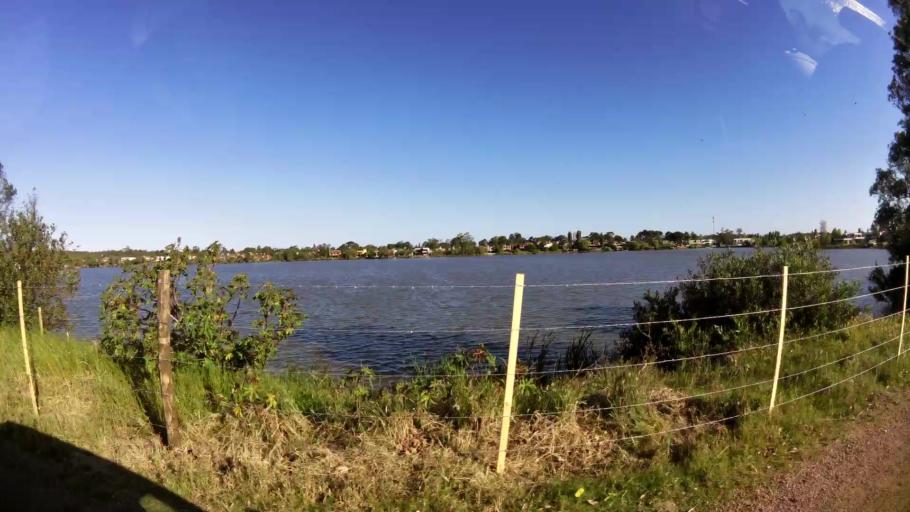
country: UY
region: Canelones
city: Paso de Carrasco
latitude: -34.8628
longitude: -56.0426
